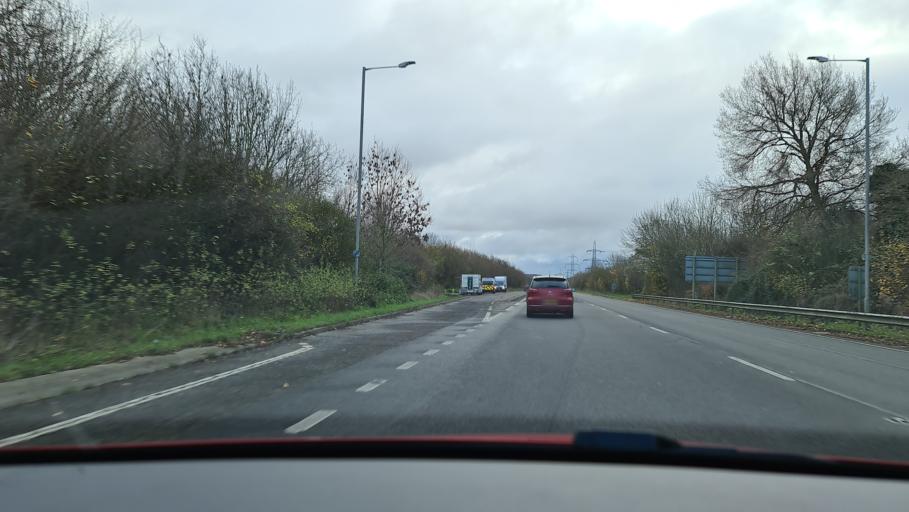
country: GB
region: England
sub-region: Buckinghamshire
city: Wendover
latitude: 51.7691
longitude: -0.7628
